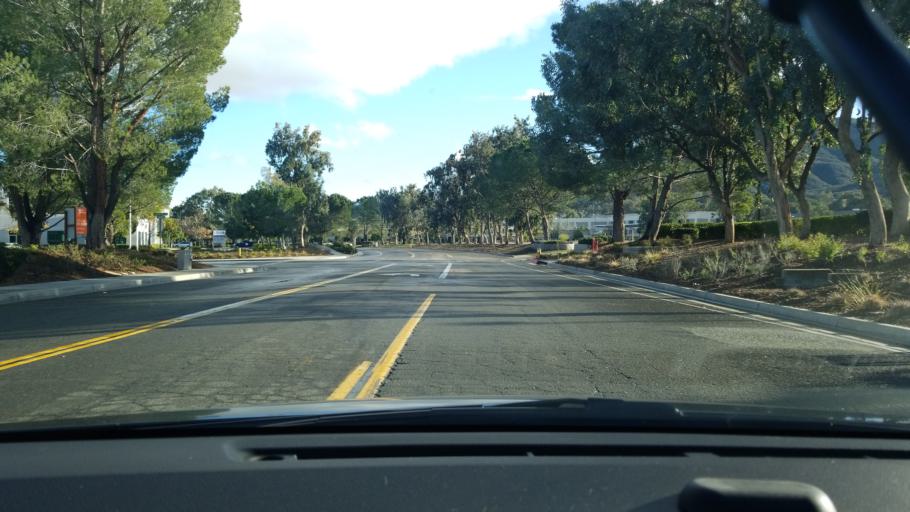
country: US
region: California
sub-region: Riverside County
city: Temecula
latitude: 33.5028
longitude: -117.1624
